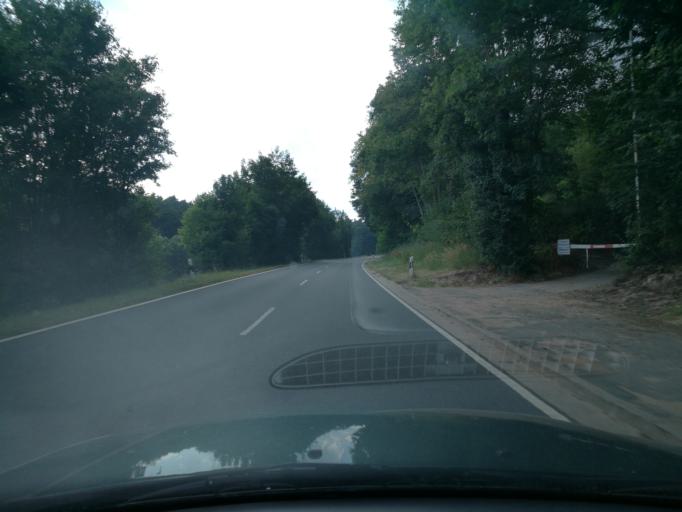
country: DE
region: Bavaria
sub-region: Regierungsbezirk Mittelfranken
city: Grosshabersdorf
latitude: 49.4072
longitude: 10.7722
